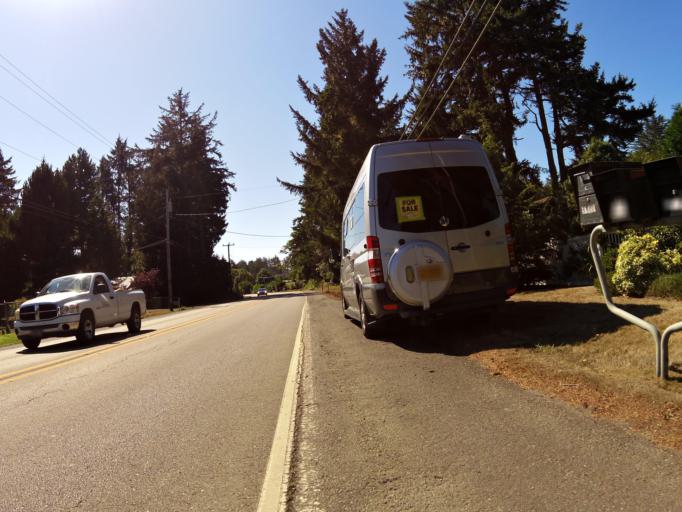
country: US
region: Oregon
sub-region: Coos County
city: Barview
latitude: 43.3528
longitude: -124.3130
